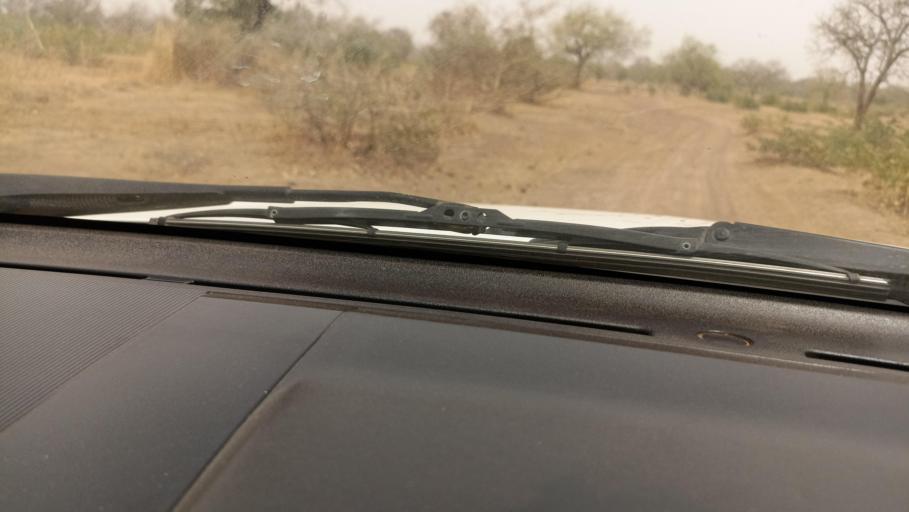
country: BF
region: Boucle du Mouhoun
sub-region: Province du Nayala
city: Toma
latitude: 12.8554
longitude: -2.8091
